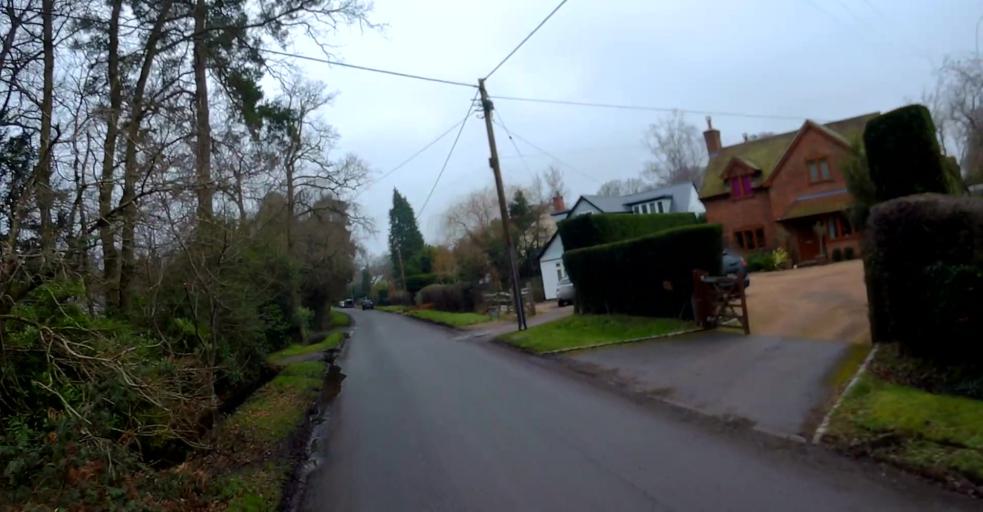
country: GB
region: England
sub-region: Hampshire
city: Eversley
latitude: 51.3531
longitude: -0.8989
